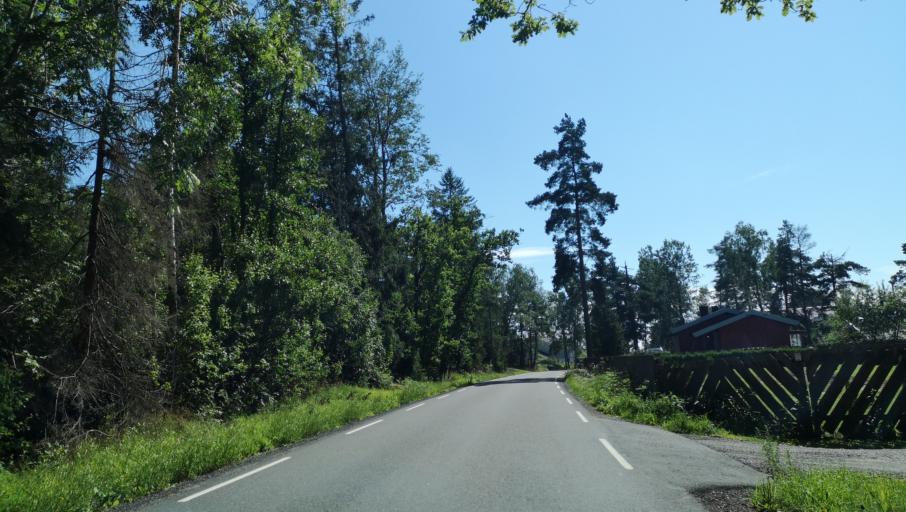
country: NO
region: Akershus
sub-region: Vestby
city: Vestby
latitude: 59.5382
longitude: 10.6905
